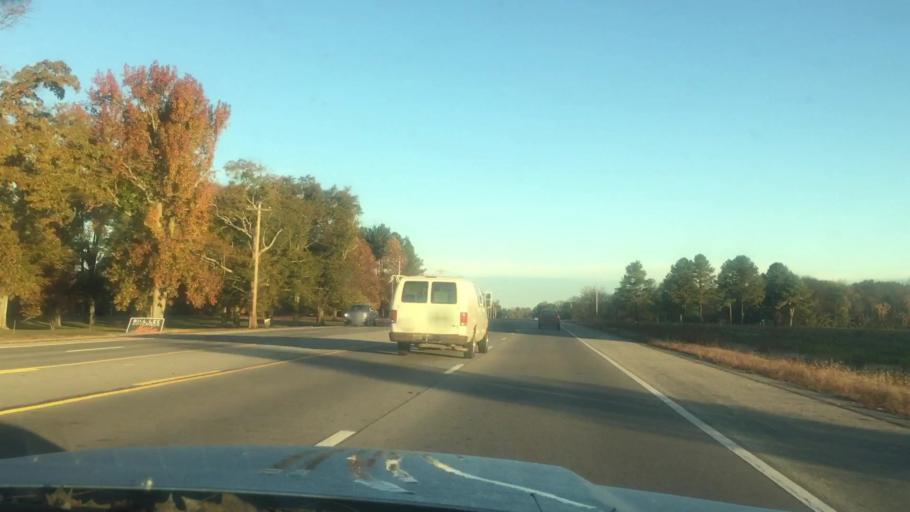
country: US
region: Tennessee
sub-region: Franklin County
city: Decherd
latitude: 35.2337
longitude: -86.1111
